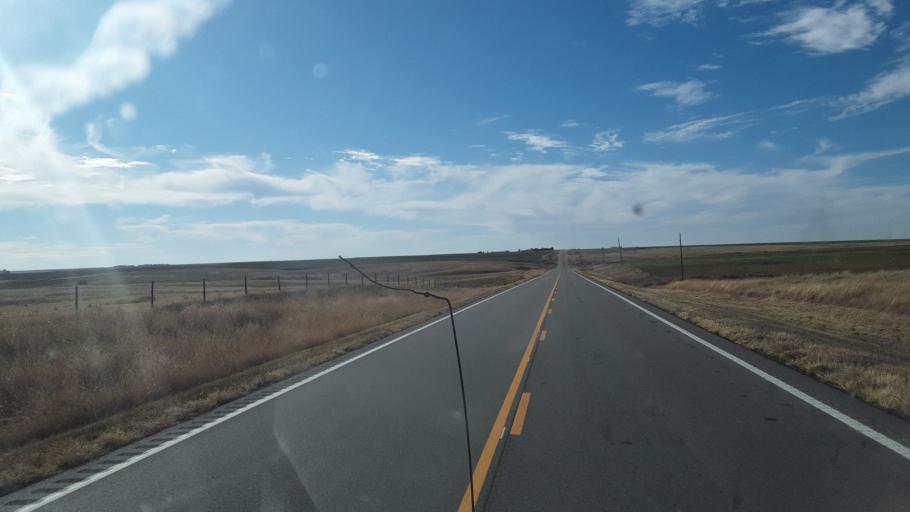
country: US
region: Kansas
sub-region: Hodgeman County
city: Jetmore
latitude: 38.0727
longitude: -100.0917
